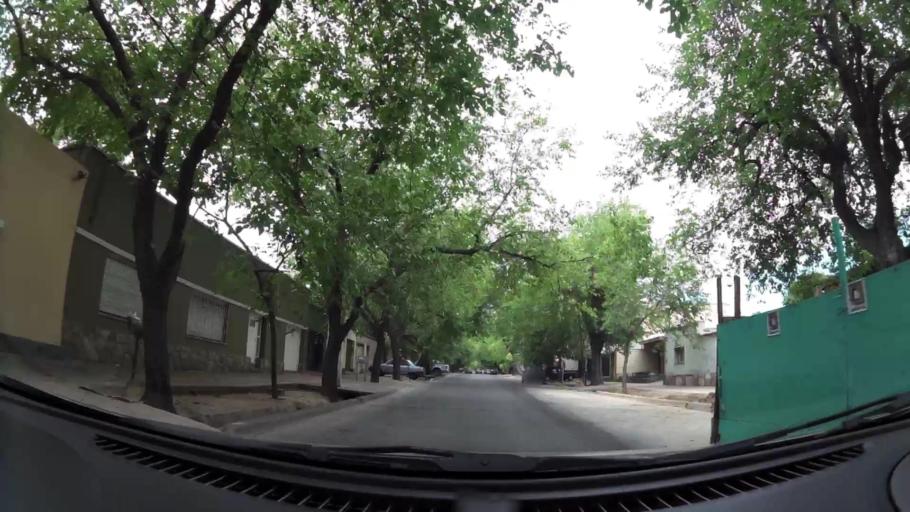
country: AR
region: Mendoza
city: Mendoza
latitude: -32.8924
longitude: -68.8568
